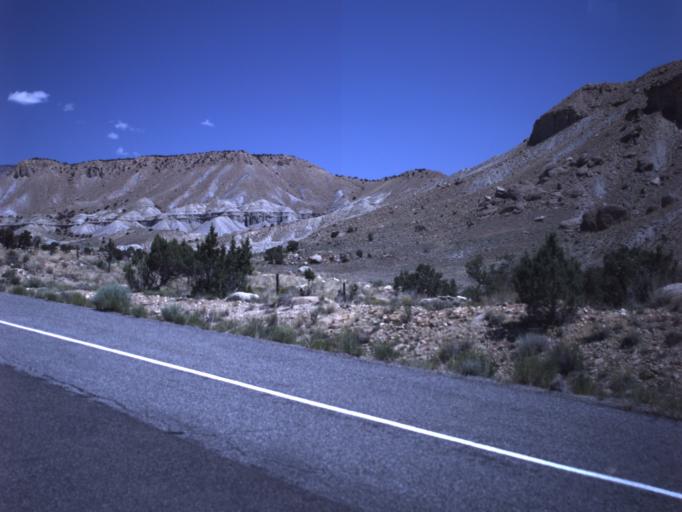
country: US
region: Utah
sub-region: Emery County
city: Orangeville
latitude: 39.2579
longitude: -111.0982
